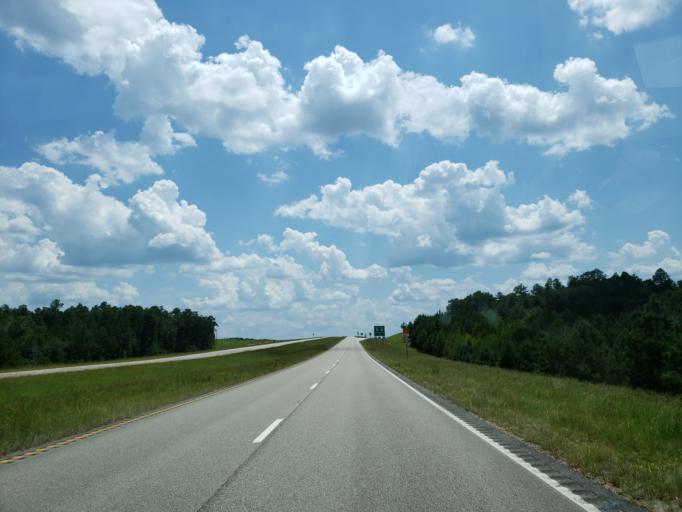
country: US
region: Mississippi
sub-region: Greene County
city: Leakesville
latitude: 31.1349
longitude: -88.5076
